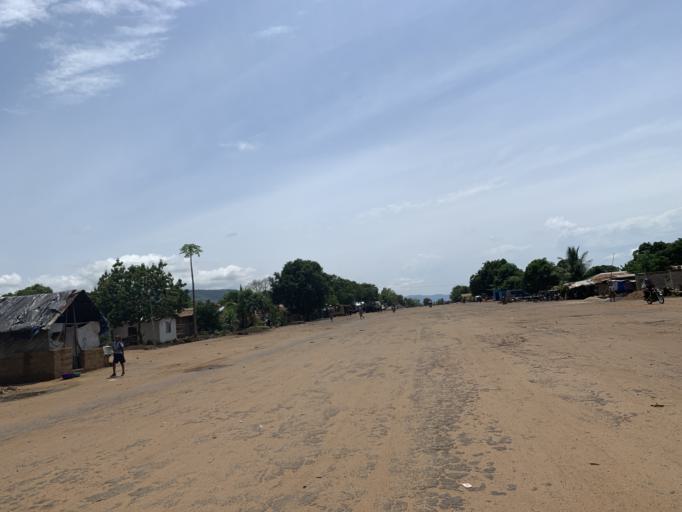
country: SL
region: Western Area
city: Waterloo
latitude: 8.3393
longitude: -13.0463
